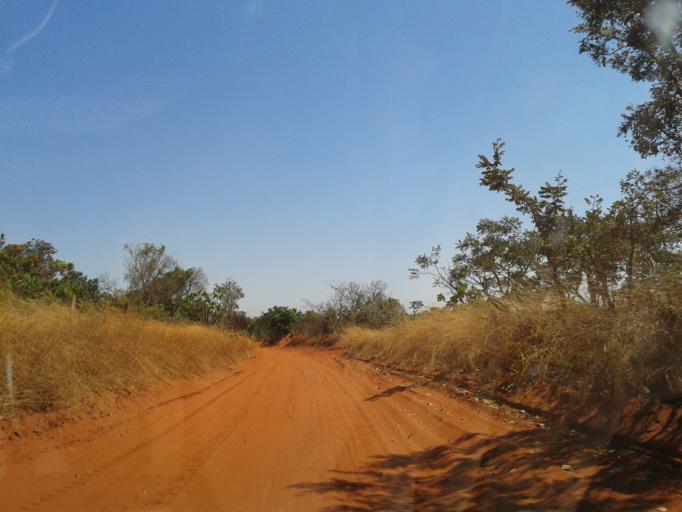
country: BR
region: Minas Gerais
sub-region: Ituiutaba
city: Ituiutaba
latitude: -19.0068
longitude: -49.3646
